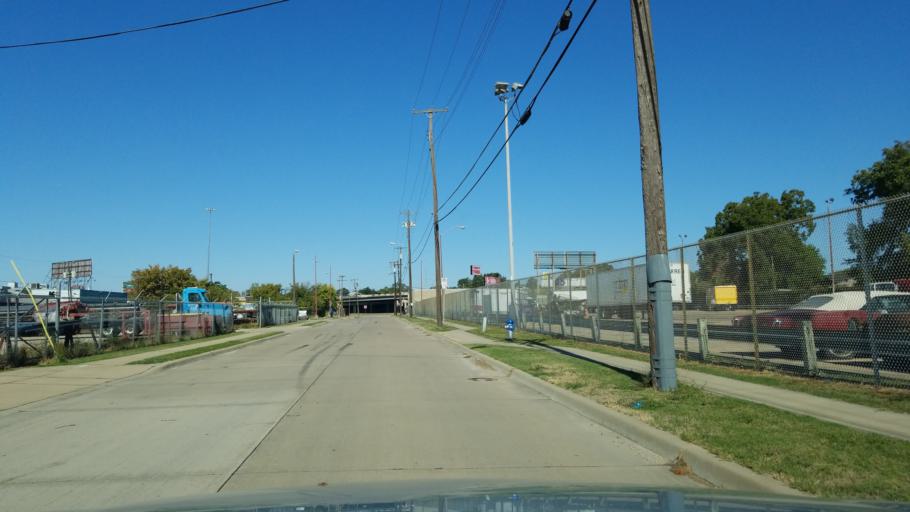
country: US
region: Texas
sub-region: Dallas County
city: Dallas
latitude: 32.7893
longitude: -96.7482
